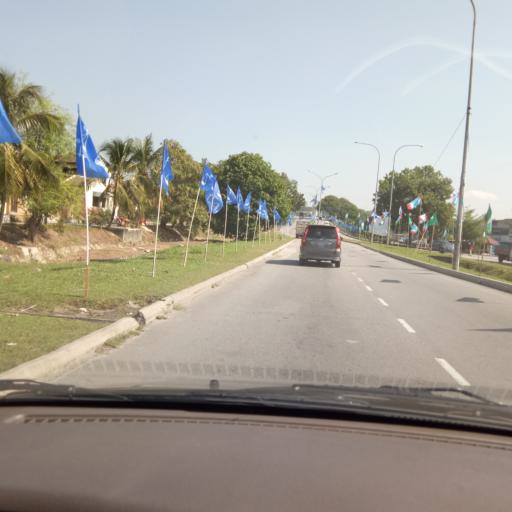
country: MY
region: Selangor
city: Kampong Baharu Balakong
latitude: 3.0274
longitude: 101.7633
